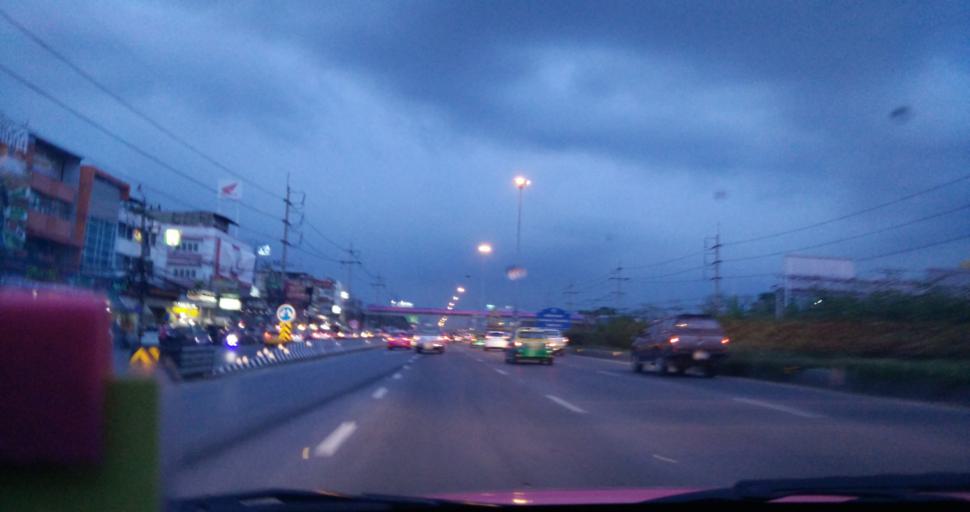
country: TH
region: Pathum Thani
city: Khlong Luang
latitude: 14.0075
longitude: 100.6151
